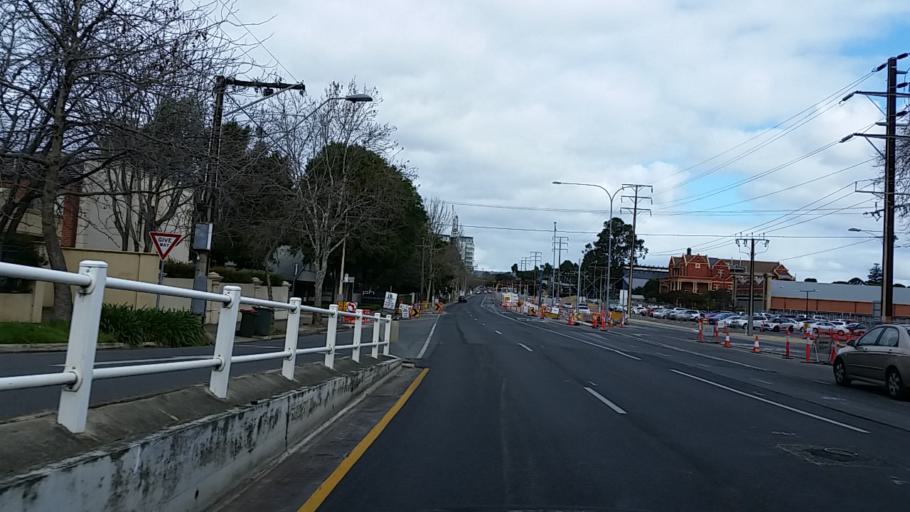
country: AU
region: South Australia
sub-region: Adelaide
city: Adelaide
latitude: -34.9154
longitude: 138.6142
